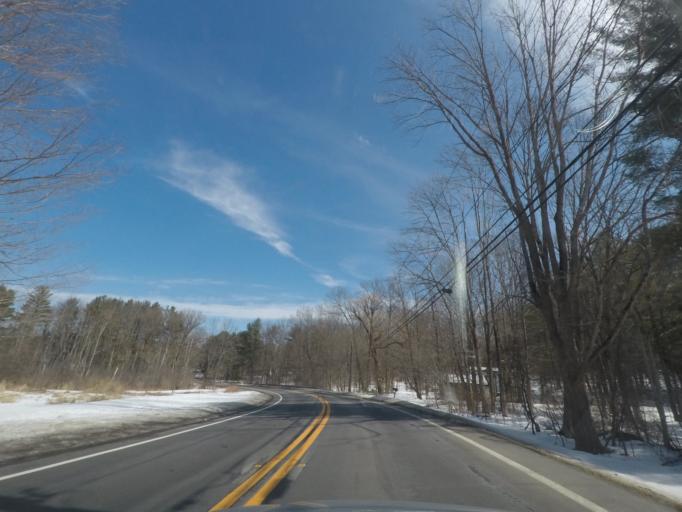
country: US
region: Massachusetts
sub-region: Berkshire County
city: Richmond
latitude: 42.3662
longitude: -73.3722
